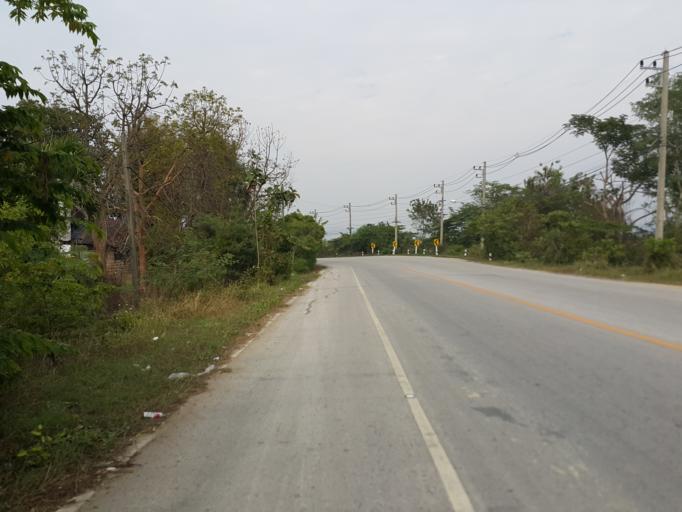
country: TH
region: Chiang Mai
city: San Kamphaeng
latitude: 18.8211
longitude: 99.1251
